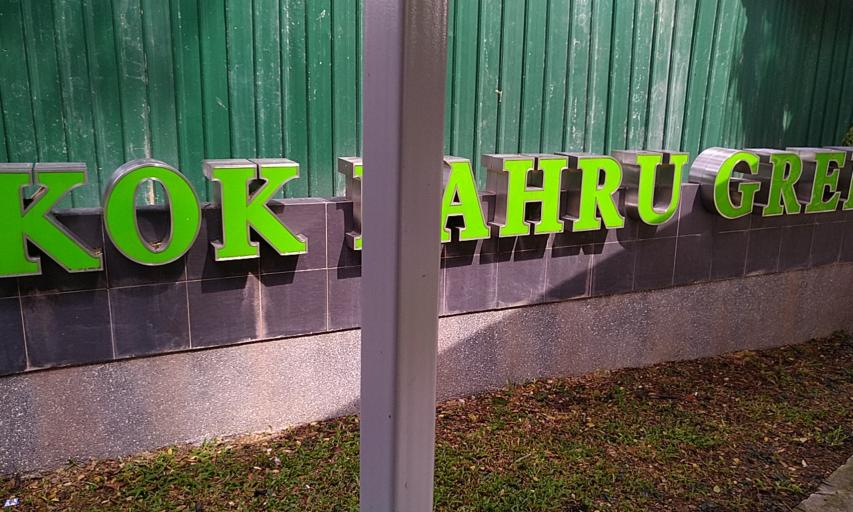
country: SG
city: Singapore
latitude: 1.2889
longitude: 103.8150
